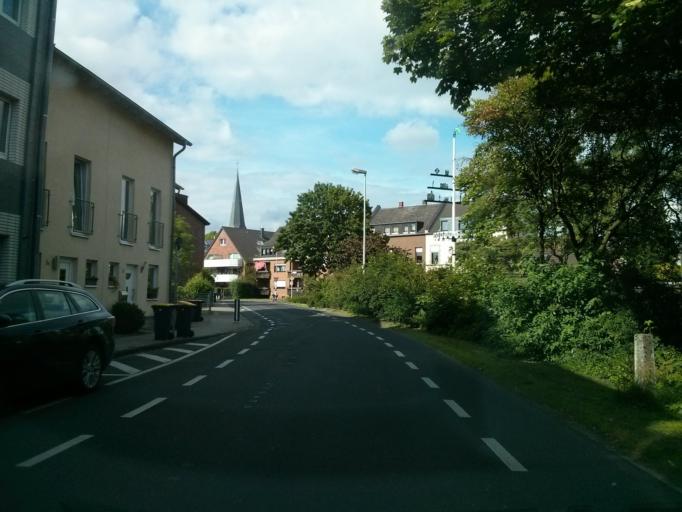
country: DE
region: North Rhine-Westphalia
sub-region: Regierungsbezirk Dusseldorf
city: Krefeld
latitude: 51.3009
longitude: 6.5855
